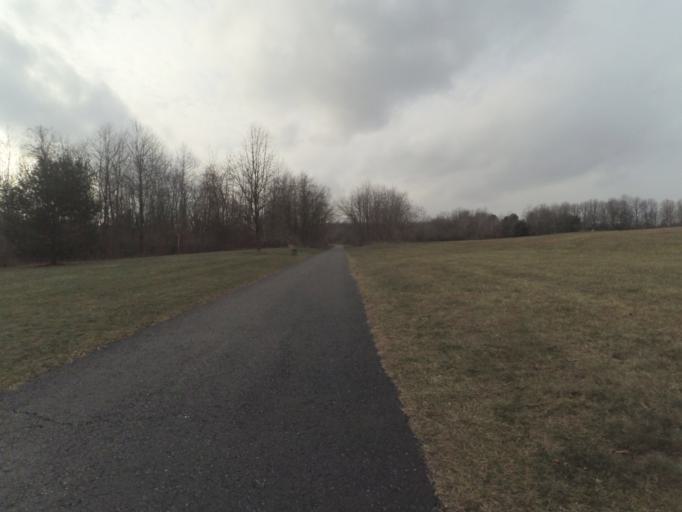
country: US
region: Pennsylvania
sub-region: Centre County
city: Park Forest Village
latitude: 40.8003
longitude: -77.8935
